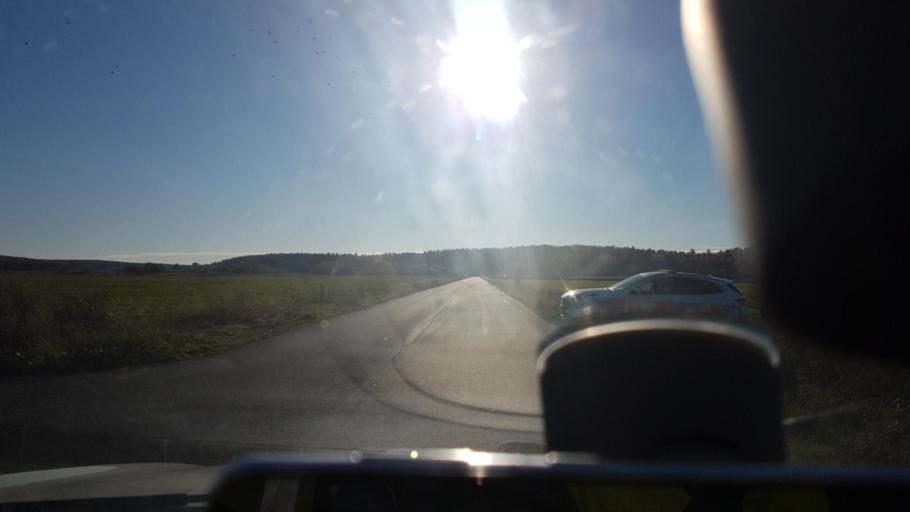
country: SE
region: Uppsala
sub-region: Uppsala Kommun
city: Uppsala
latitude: 59.8404
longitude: 17.6693
